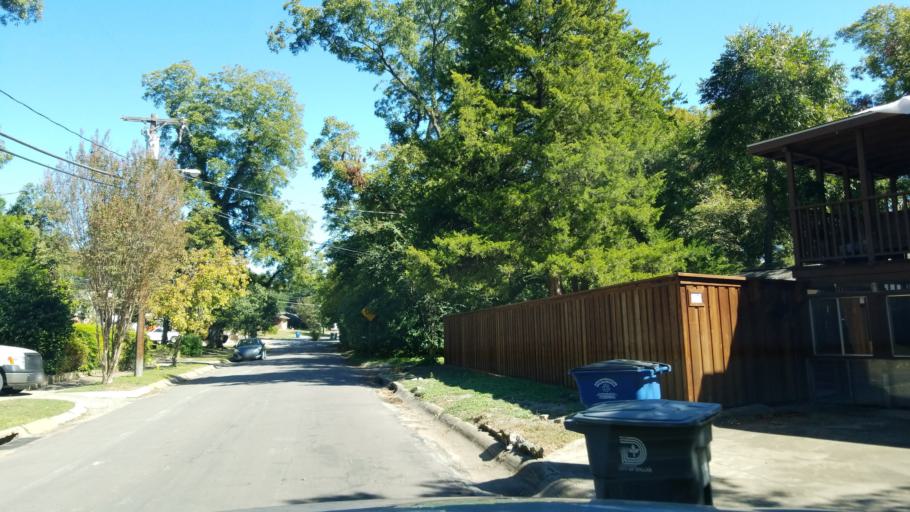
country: US
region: Texas
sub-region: Dallas County
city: Highland Park
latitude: 32.8088
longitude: -96.7416
